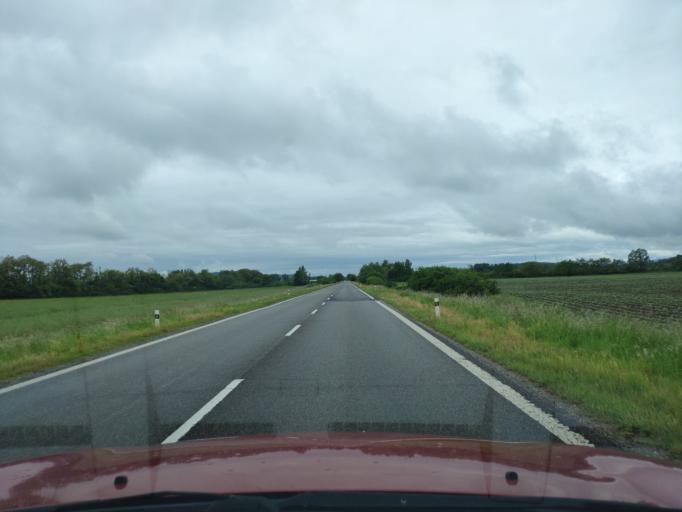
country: HU
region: Borsod-Abauj-Zemplen
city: Karcsa
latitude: 48.4210
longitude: 21.8362
